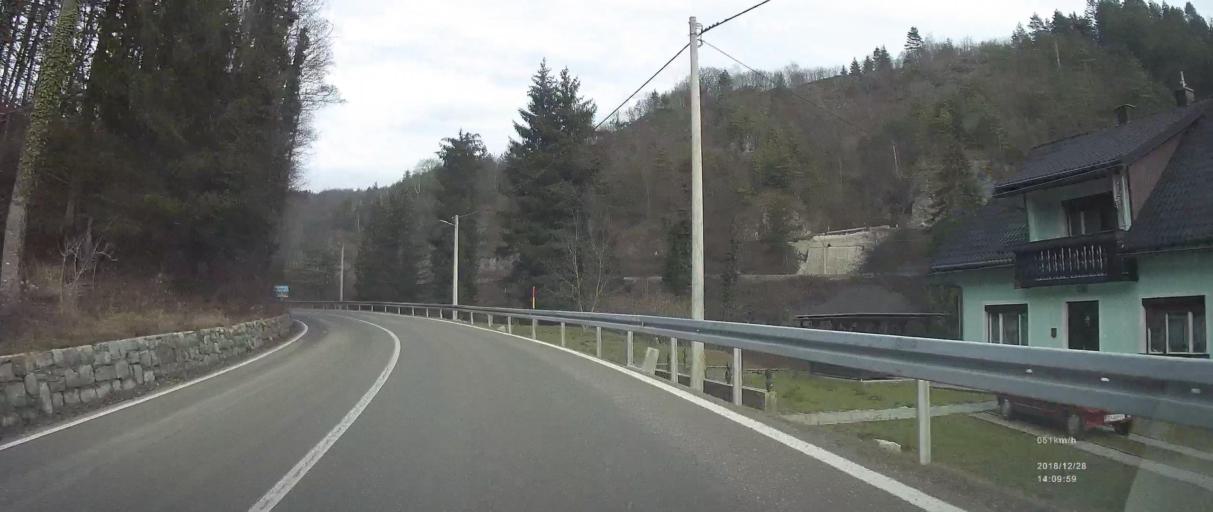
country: SI
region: Kostel
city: Kostel
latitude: 45.4497
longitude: 14.9775
